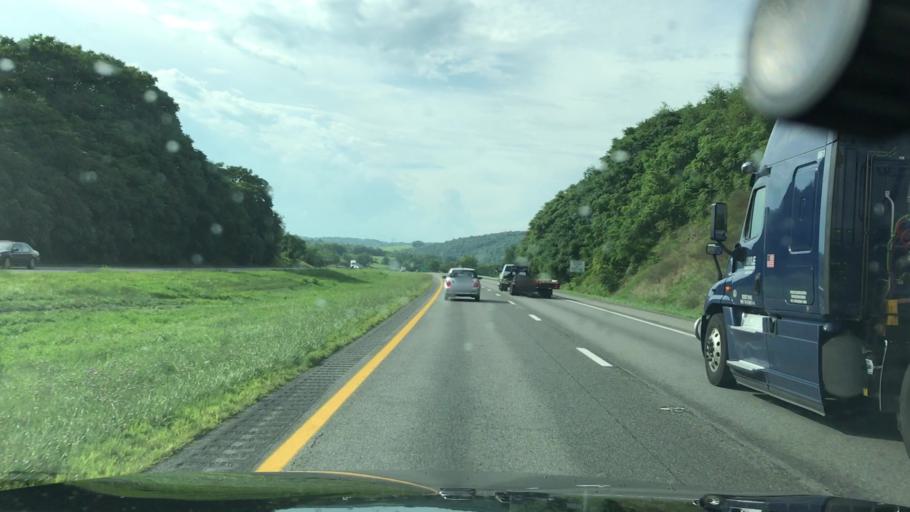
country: US
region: Virginia
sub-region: Carroll County
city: Woodlawn
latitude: 36.8568
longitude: -80.8648
